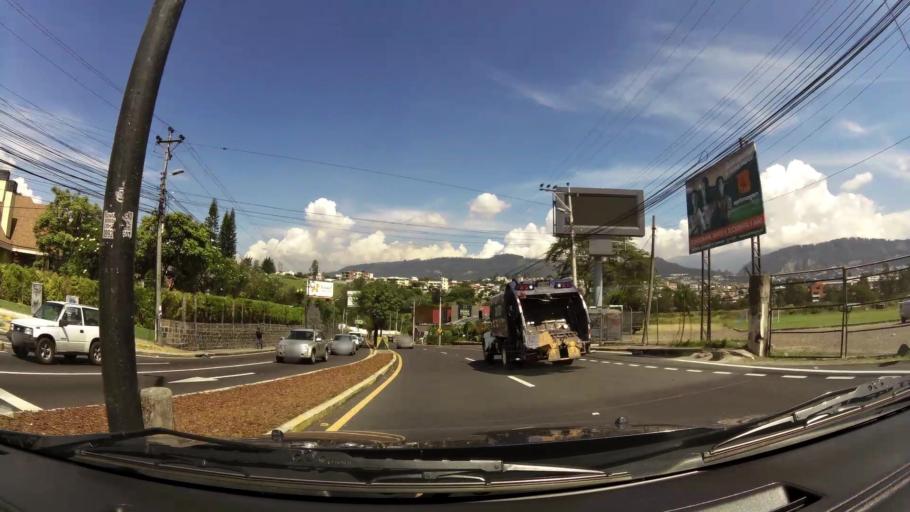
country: EC
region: Pichincha
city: Quito
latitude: -0.2106
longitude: -78.4209
